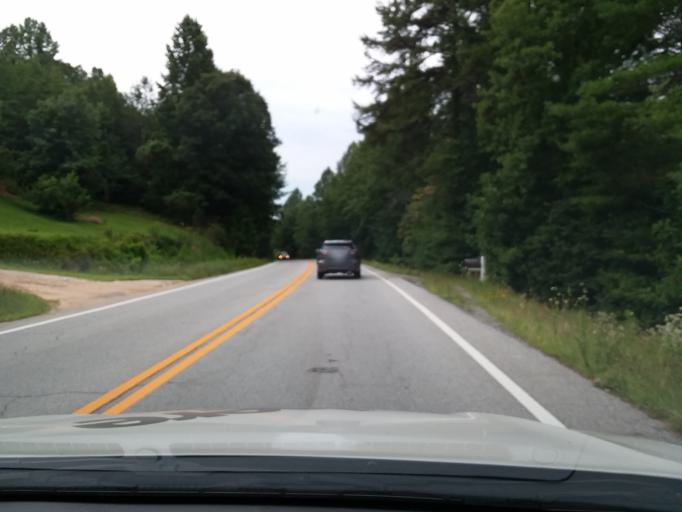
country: US
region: Georgia
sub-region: Rabun County
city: Clayton
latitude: 34.8270
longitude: -83.3222
